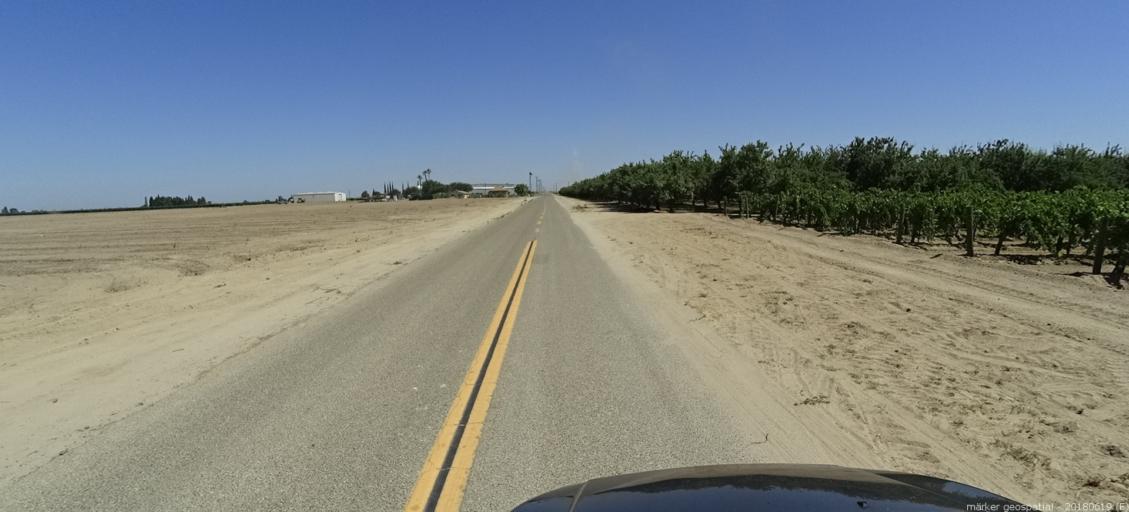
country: US
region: California
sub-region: Fresno County
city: Biola
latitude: 36.8373
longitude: -120.0649
